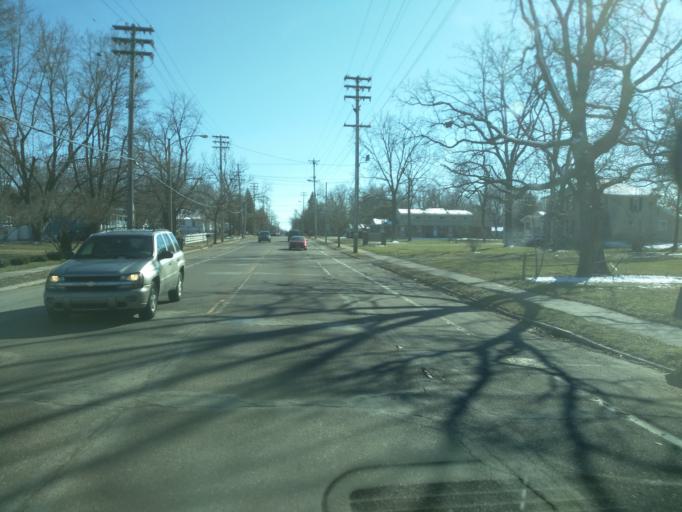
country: US
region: Michigan
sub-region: Ingham County
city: Lansing
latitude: 42.6941
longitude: -84.5823
